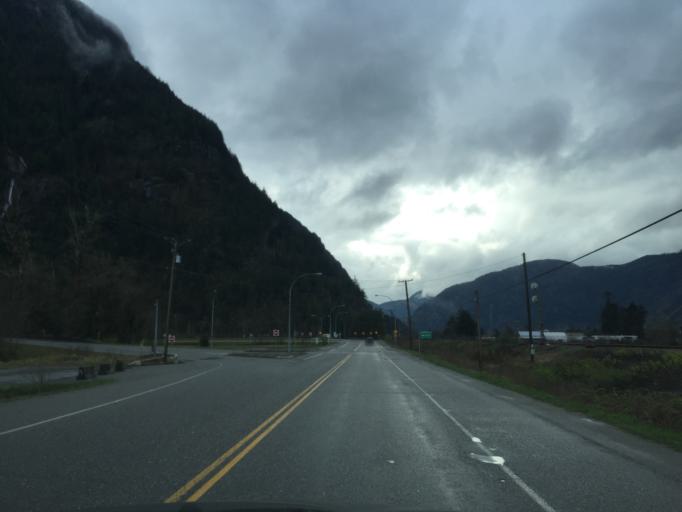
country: CA
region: British Columbia
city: Hope
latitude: 49.3655
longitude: -121.5187
